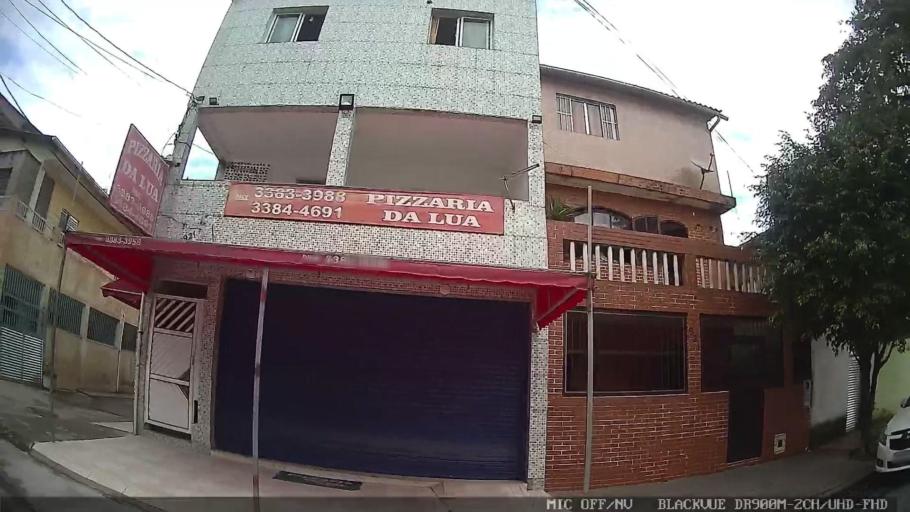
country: BR
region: Sao Paulo
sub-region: Guaruja
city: Guaruja
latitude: -23.9892
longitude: -46.2831
